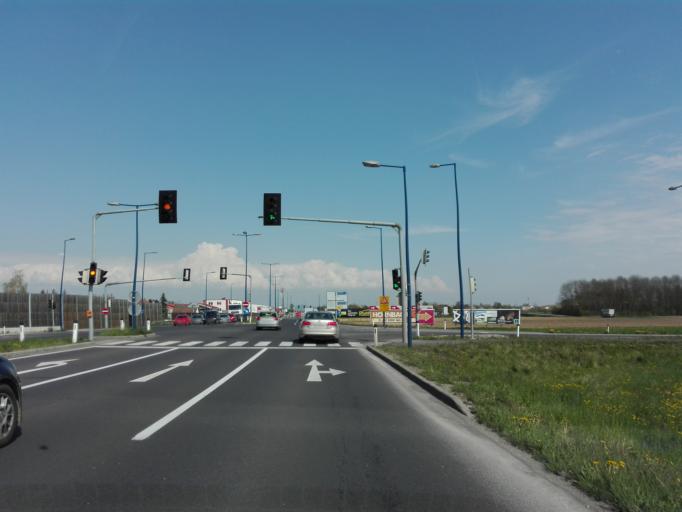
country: AT
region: Upper Austria
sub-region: Politischer Bezirk Linz-Land
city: Traun
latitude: 48.2291
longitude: 14.2174
